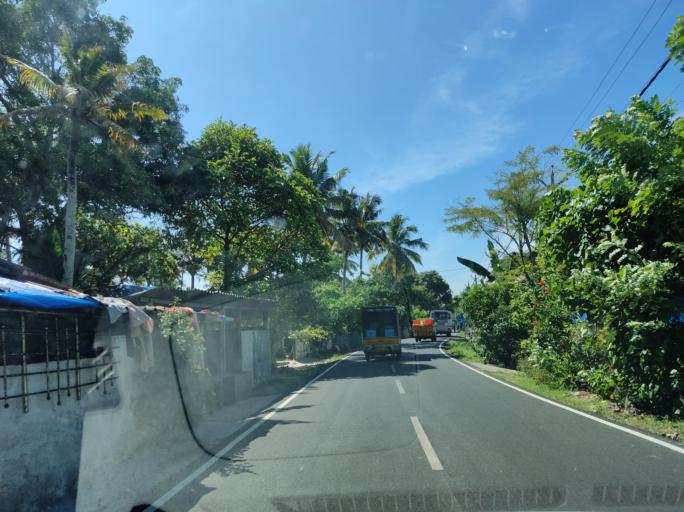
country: IN
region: Kerala
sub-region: Alappuzha
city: Kayankulam
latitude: 9.1742
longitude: 76.4462
